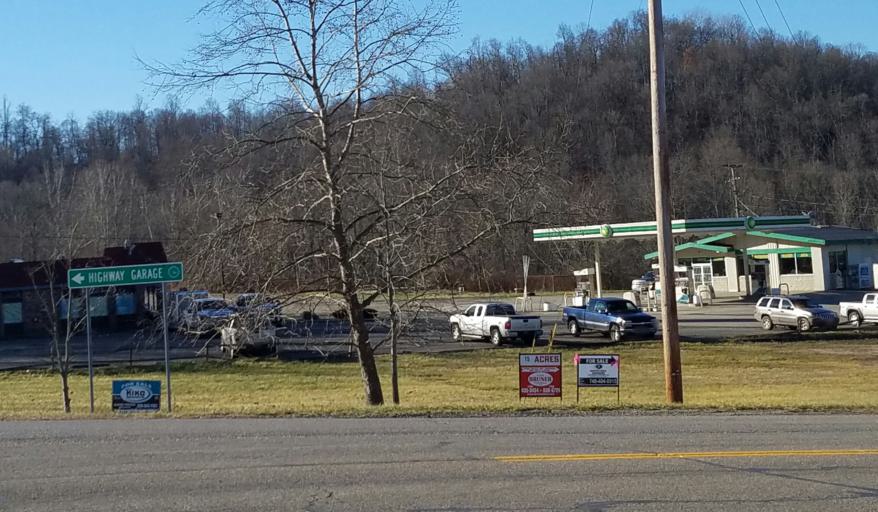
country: US
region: Ohio
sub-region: Guernsey County
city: Cambridge
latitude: 40.1462
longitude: -81.5513
